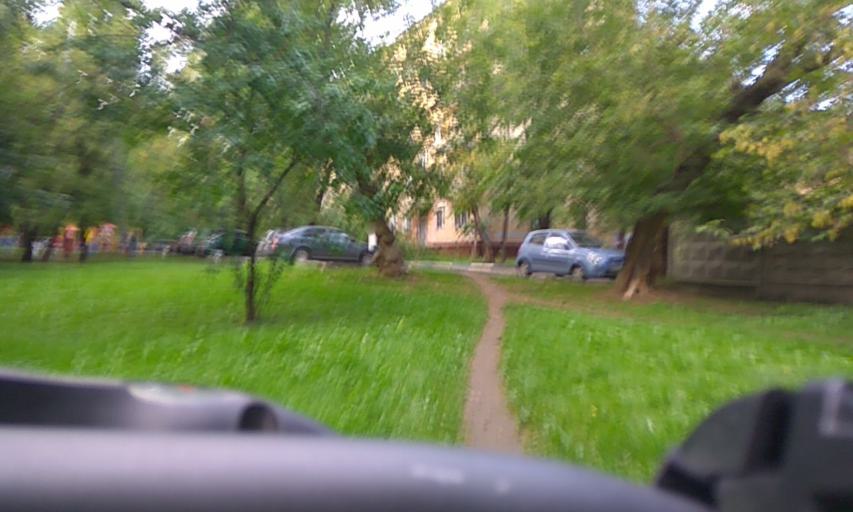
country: RU
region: Moscow
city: Kolomenskoye
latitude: 55.6812
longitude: 37.6902
